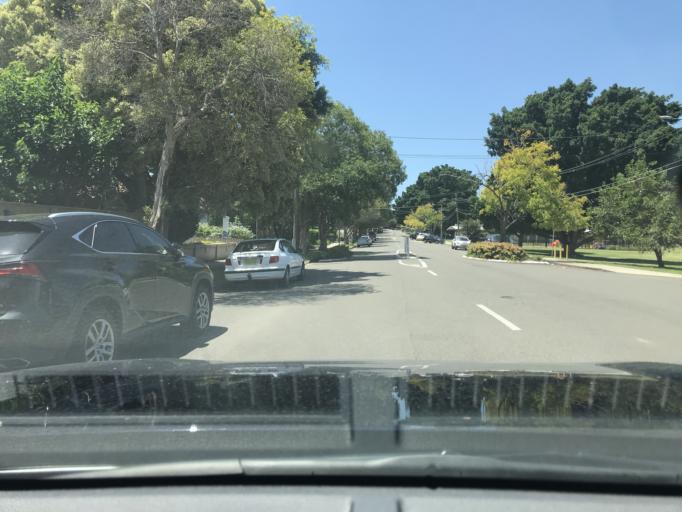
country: AU
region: New South Wales
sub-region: Canada Bay
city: Concord
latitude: -33.8540
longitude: 151.1046
